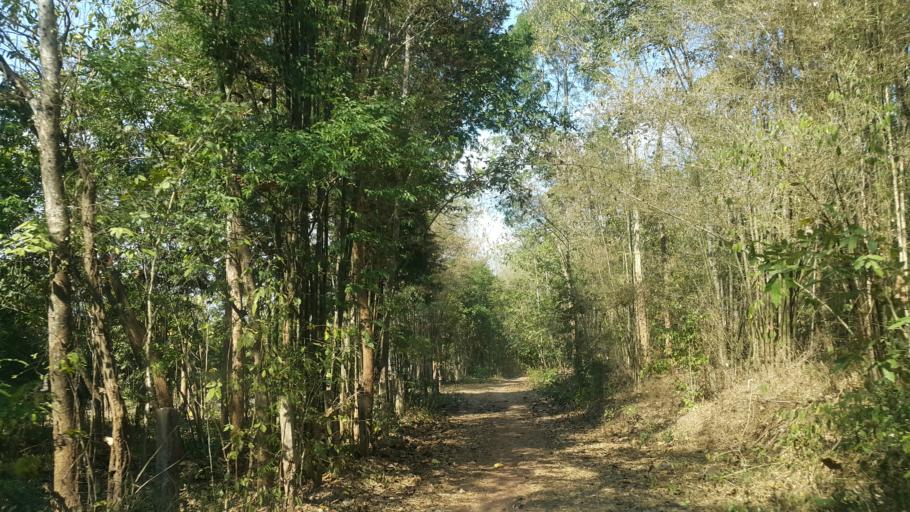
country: TH
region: Sukhothai
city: Thung Saliam
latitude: 17.3554
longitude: 99.5783
